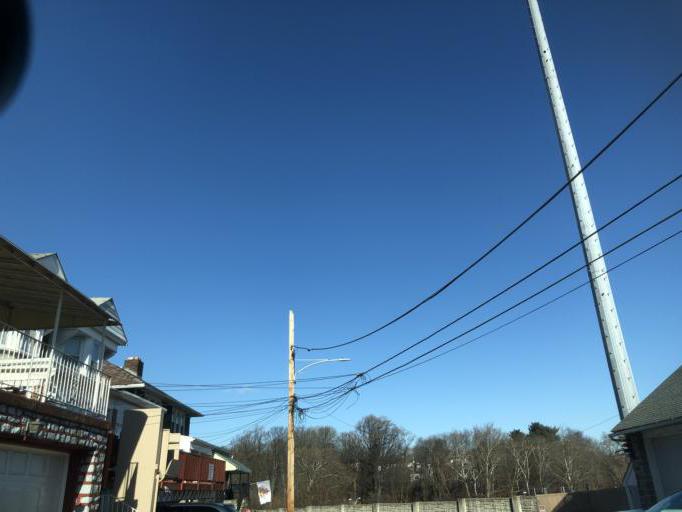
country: US
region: Pennsylvania
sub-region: Delaware County
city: Millbourne
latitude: 39.9636
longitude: -75.2503
